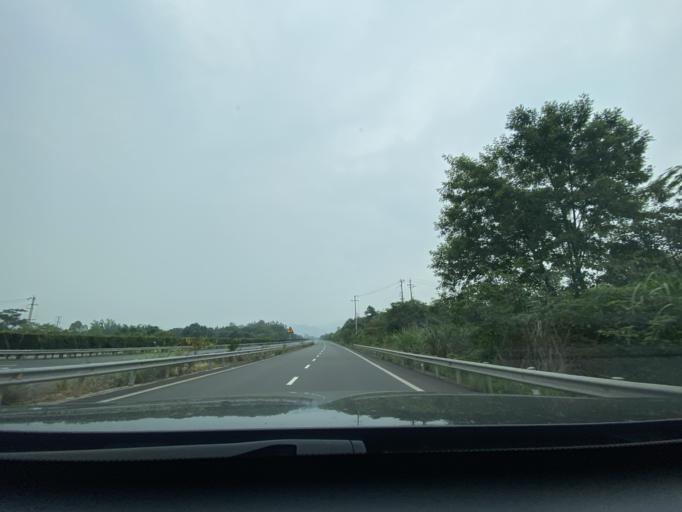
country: CN
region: Sichuan
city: Longquan
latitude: 30.3439
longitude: 104.1220
